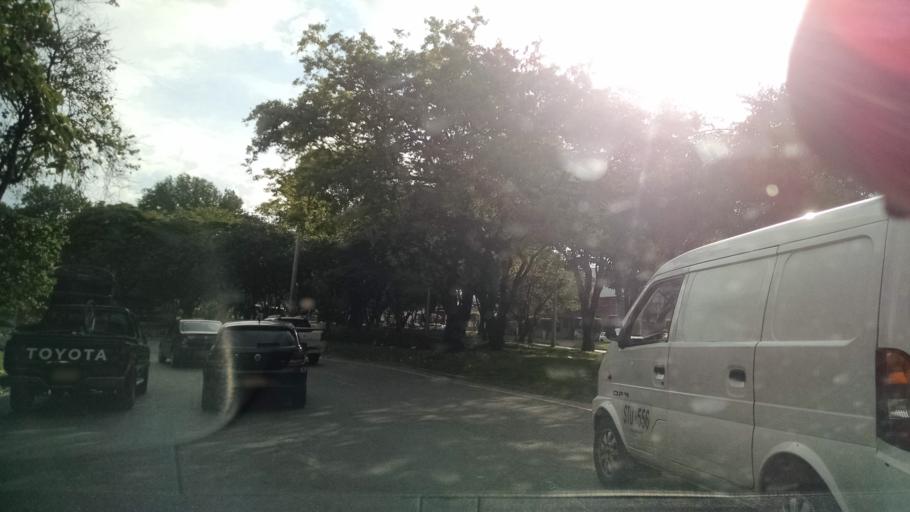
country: CO
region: Antioquia
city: Medellin
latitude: 6.2503
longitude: -75.5809
